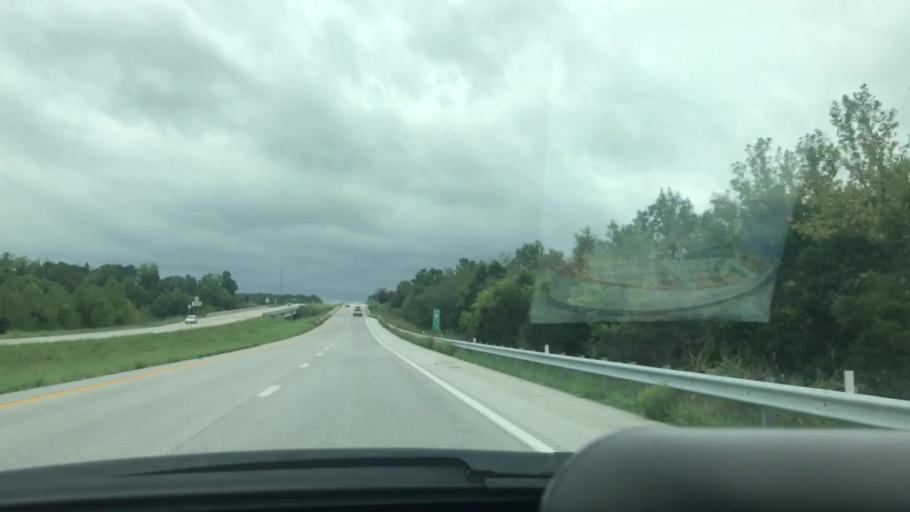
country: US
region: Missouri
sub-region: Greene County
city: Fair Grove
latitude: 37.4134
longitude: -93.1452
